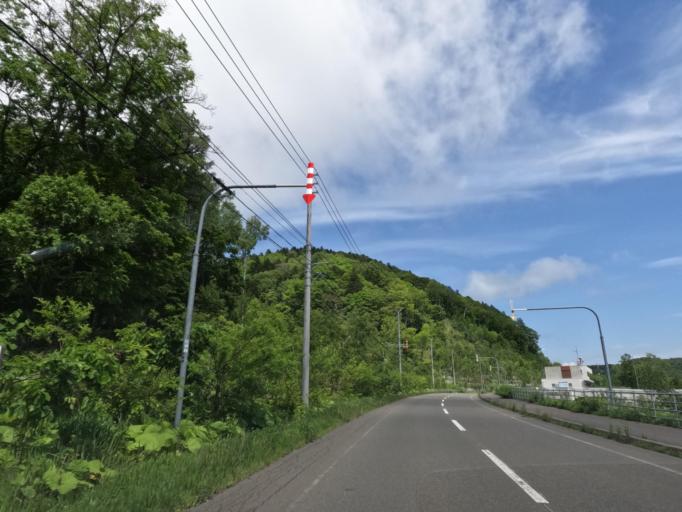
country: JP
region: Hokkaido
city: Tobetsu
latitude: 43.3192
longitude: 141.5607
